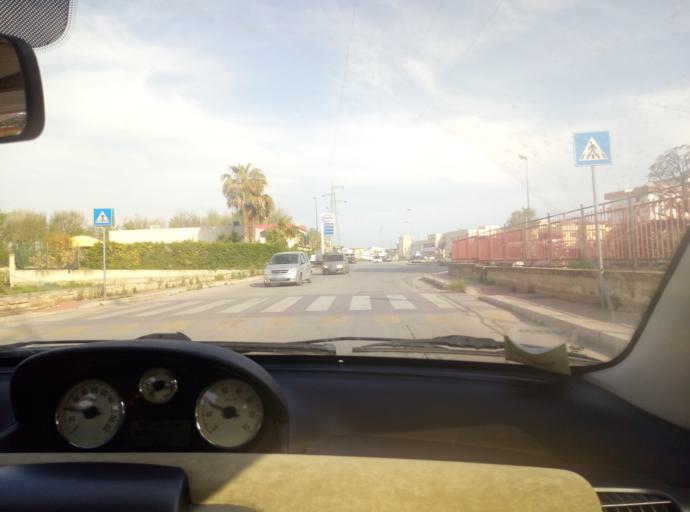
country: IT
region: Apulia
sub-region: Provincia di Bari
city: Corato
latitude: 41.1443
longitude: 16.4059
